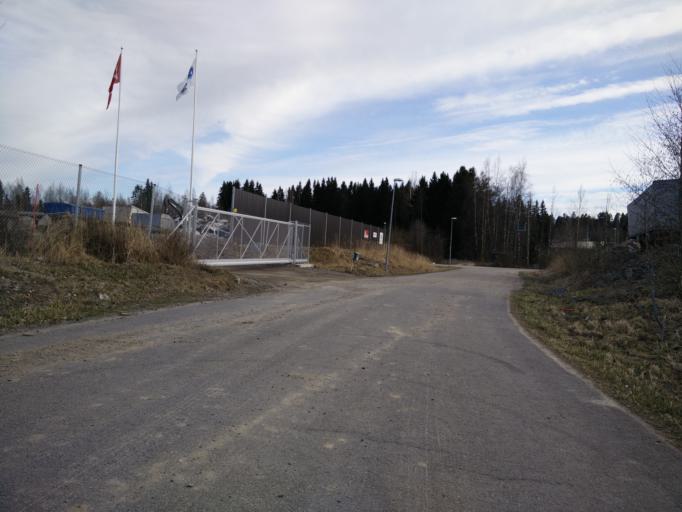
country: FI
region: Pirkanmaa
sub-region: Tampere
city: Orivesi
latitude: 61.6969
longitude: 24.3520
